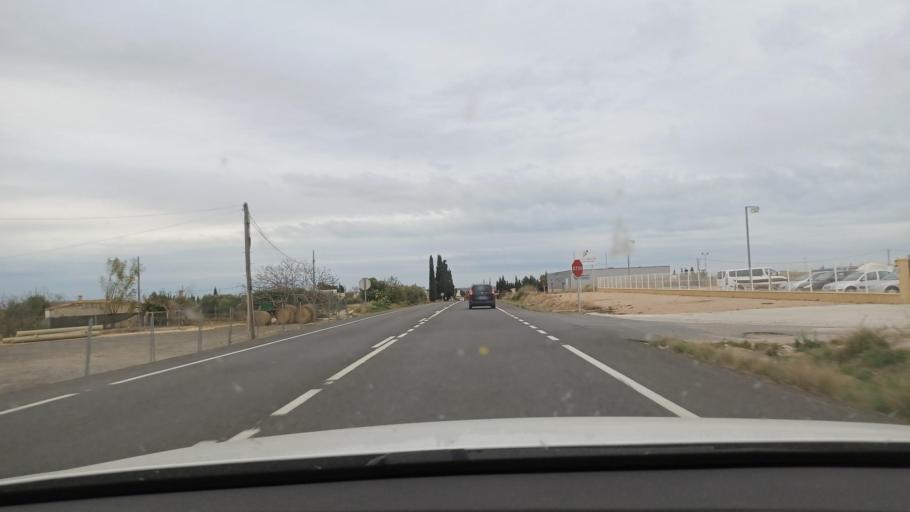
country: ES
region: Catalonia
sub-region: Provincia de Tarragona
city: Amposta
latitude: 40.6983
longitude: 0.5710
